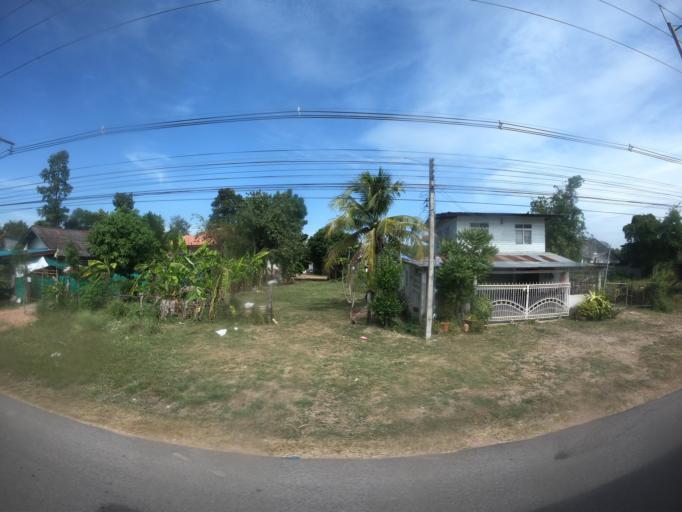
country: TH
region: Maha Sarakham
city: Chiang Yuen
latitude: 16.4440
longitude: 103.0046
